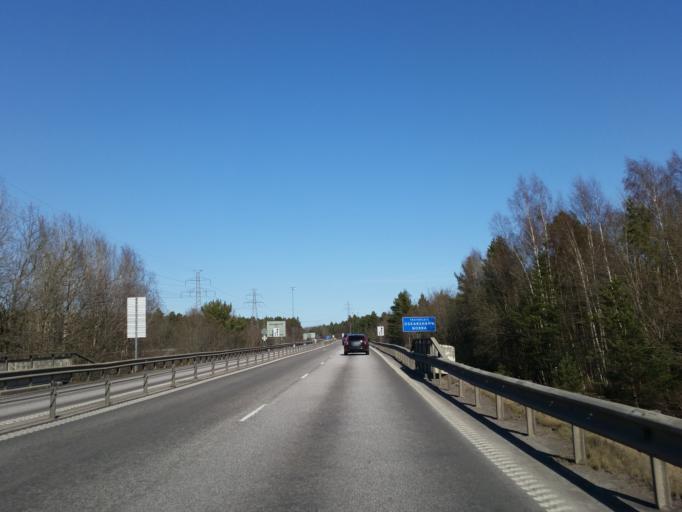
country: SE
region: Kalmar
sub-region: Oskarshamns Kommun
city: Oskarshamn
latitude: 57.2739
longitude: 16.4423
